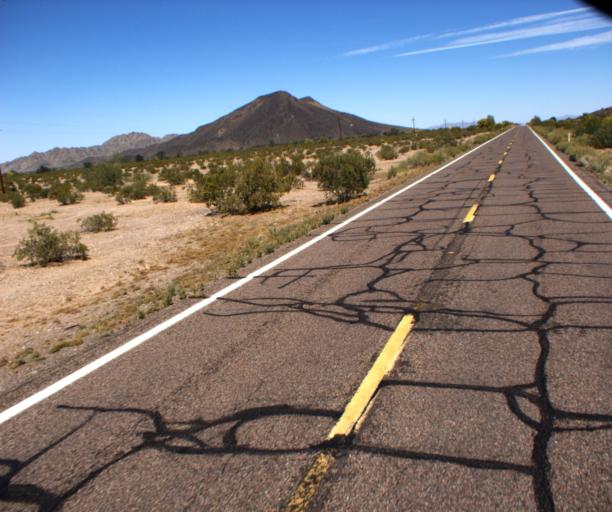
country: US
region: Arizona
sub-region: Maricopa County
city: Gila Bend
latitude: 32.7425
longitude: -112.8300
